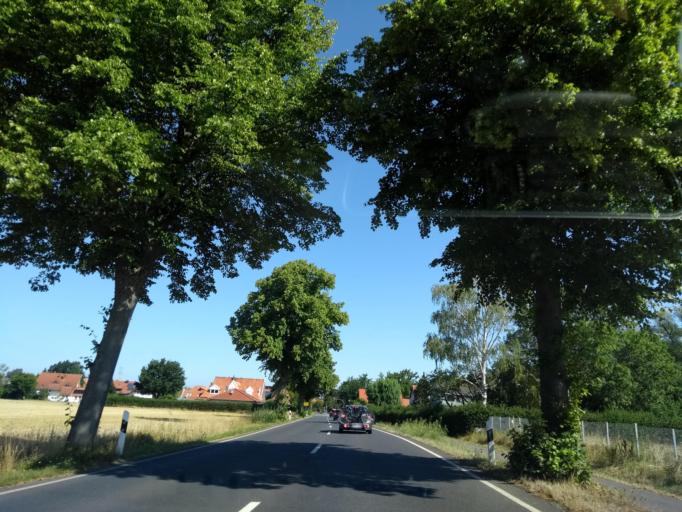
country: DE
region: Lower Saxony
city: Bad Nenndorf
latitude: 52.3524
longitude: 9.3876
